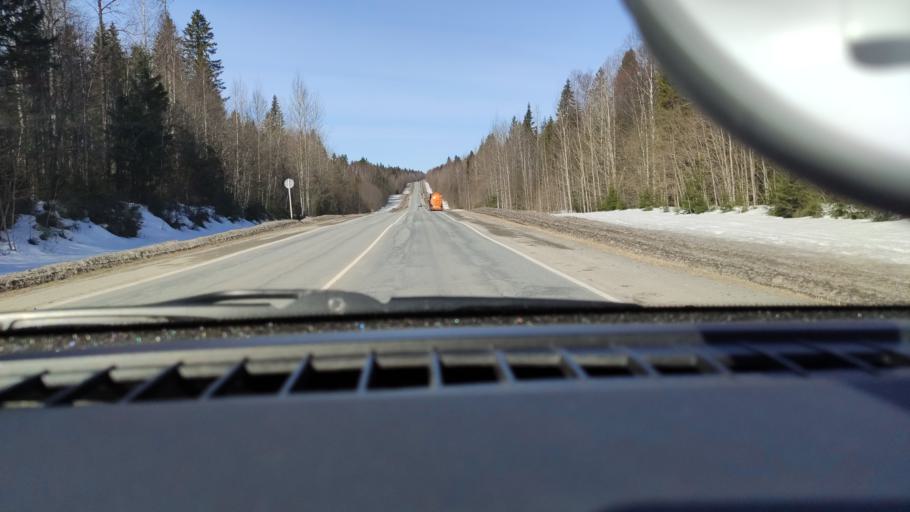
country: RU
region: Perm
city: Perm
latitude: 58.1597
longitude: 56.2468
